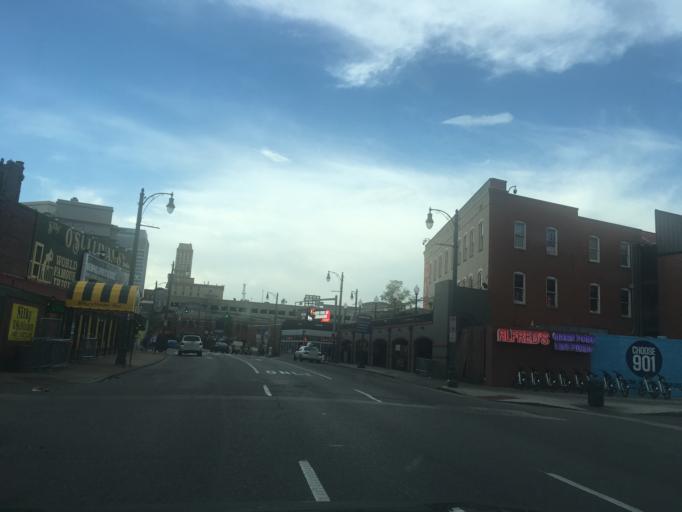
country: US
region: Tennessee
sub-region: Shelby County
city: Memphis
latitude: 35.1389
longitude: -90.0521
